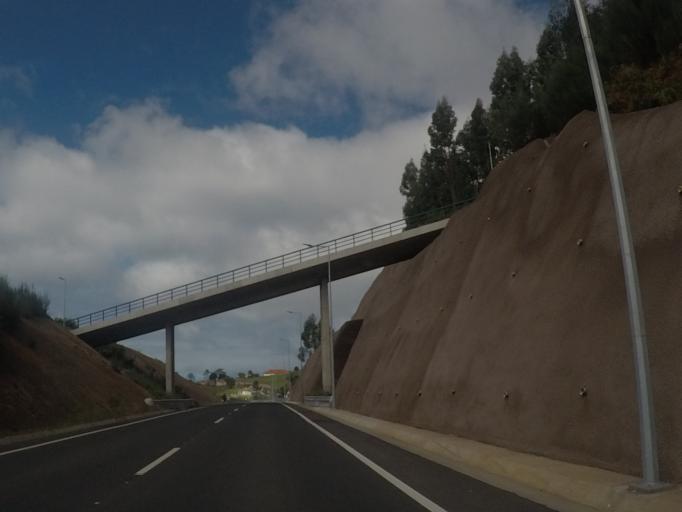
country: PT
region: Madeira
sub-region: Calheta
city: Faja da Ovelha
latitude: 32.7961
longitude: -17.2328
